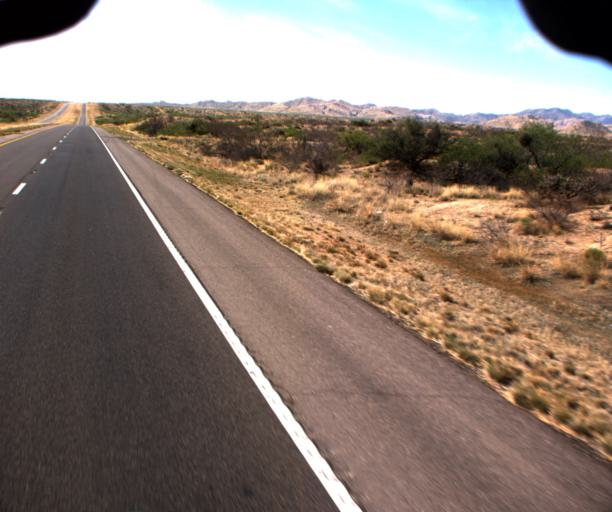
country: US
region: Arizona
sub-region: Graham County
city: Swift Trail Junction
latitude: 32.5913
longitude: -109.6843
